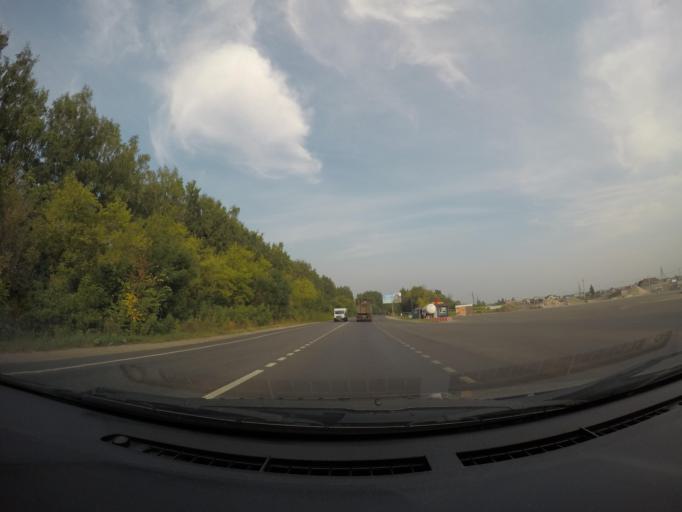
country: RU
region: Moskovskaya
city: Rechitsy
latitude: 55.5887
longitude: 38.5330
